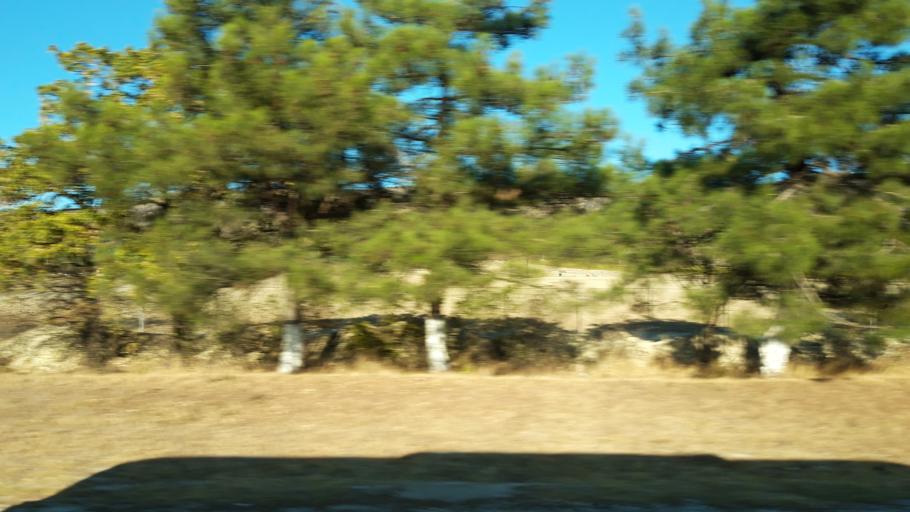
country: RU
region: Krasnodarskiy
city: Kabardinka
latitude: 44.6295
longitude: 38.0038
